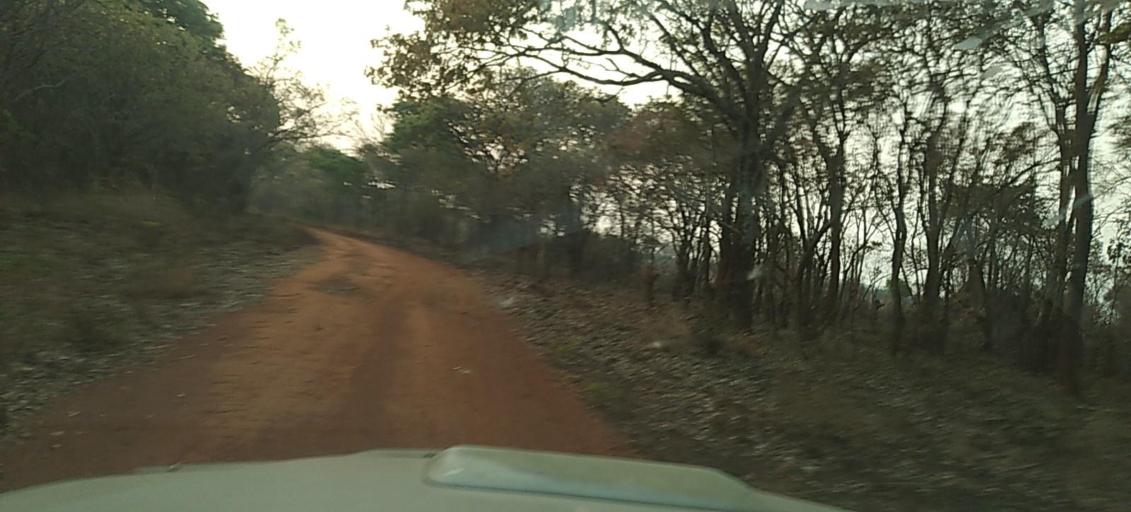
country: ZM
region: North-Western
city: Kasempa
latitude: -13.0776
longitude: 26.3909
